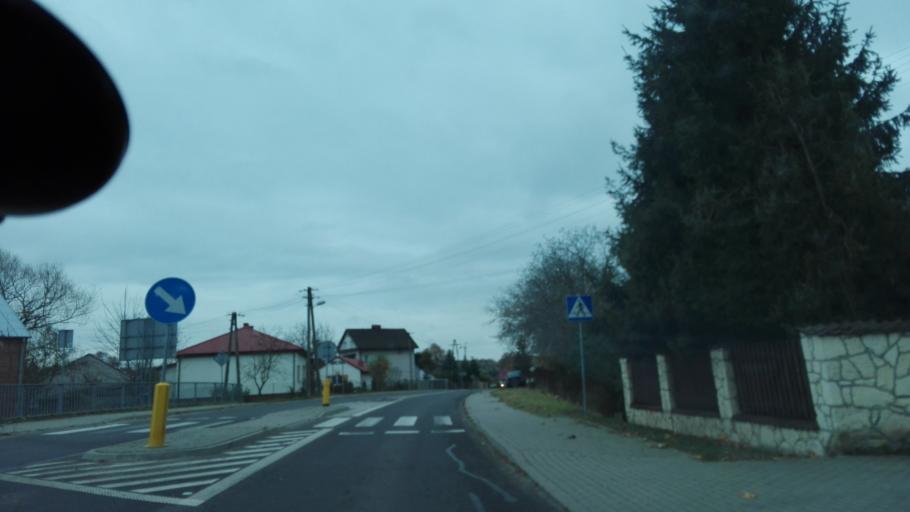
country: PL
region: Lublin Voivodeship
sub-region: Powiat pulawski
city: Pulawy
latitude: 51.4360
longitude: 21.9123
